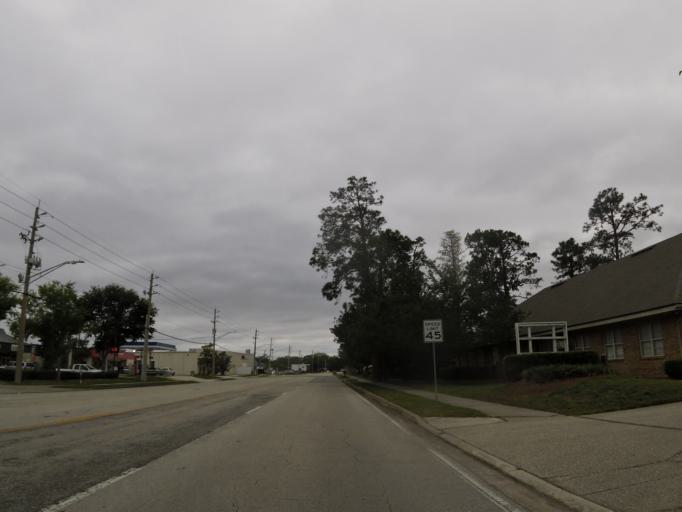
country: US
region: Florida
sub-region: Saint Johns County
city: Fruit Cove
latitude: 30.1995
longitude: -81.6151
